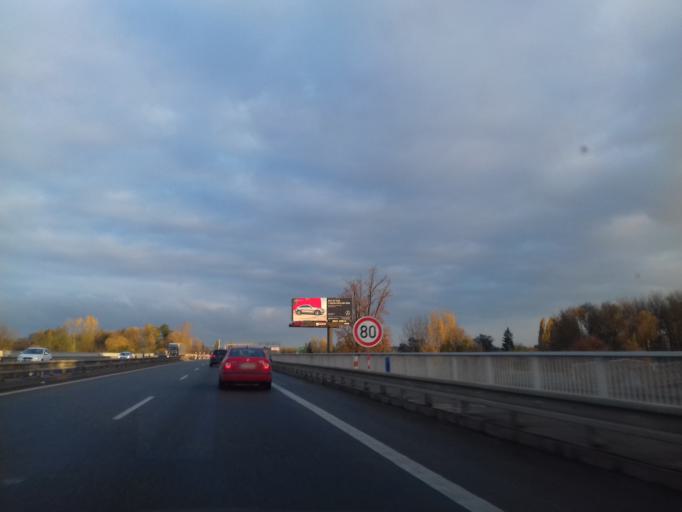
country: CZ
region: Olomoucky
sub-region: Okres Prostejov
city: Prostejov
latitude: 49.4763
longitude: 17.1319
